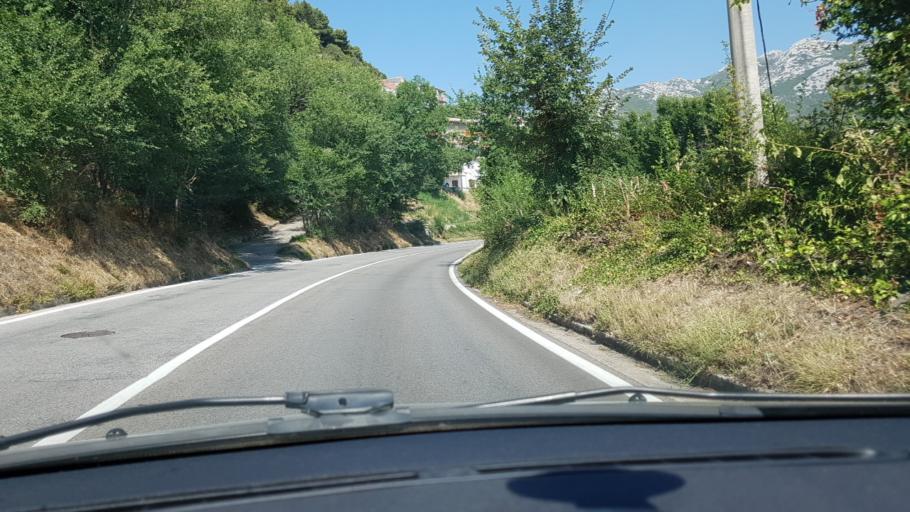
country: HR
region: Splitsko-Dalmatinska
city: Klis
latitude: 43.5584
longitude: 16.5193
